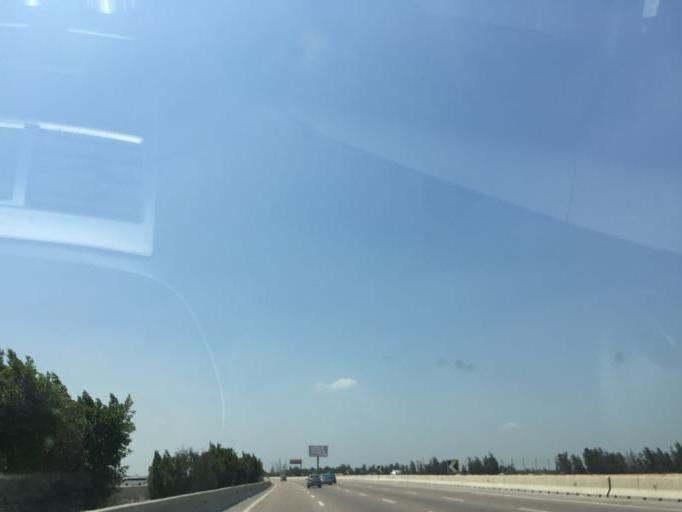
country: EG
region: Al Buhayrah
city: Beheira
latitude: 30.4402
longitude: 30.3296
